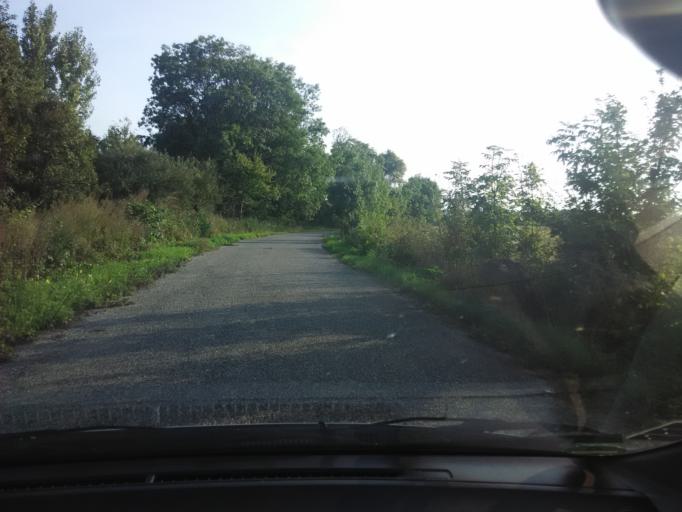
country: SK
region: Banskobystricky
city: Nova Bana
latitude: 48.3077
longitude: 18.7010
